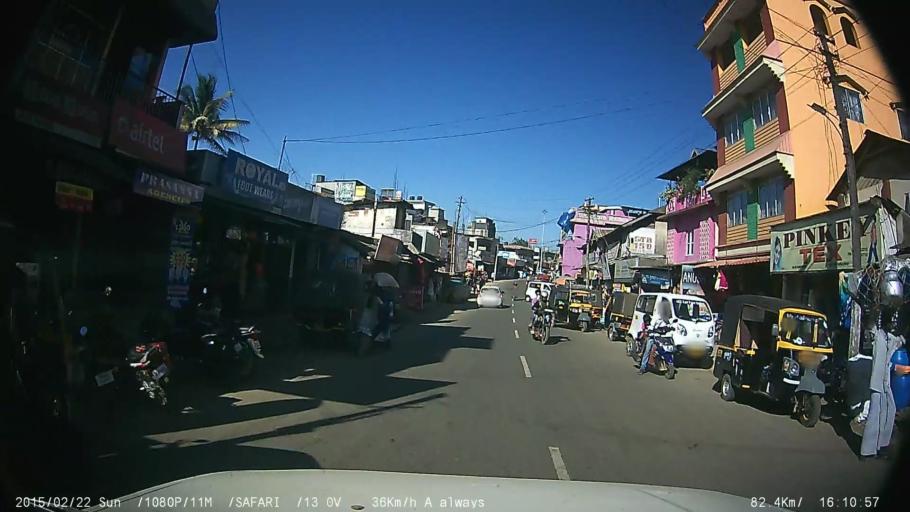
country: IN
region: Tamil Nadu
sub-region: Theni
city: Gudalur
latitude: 9.5715
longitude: 77.0892
